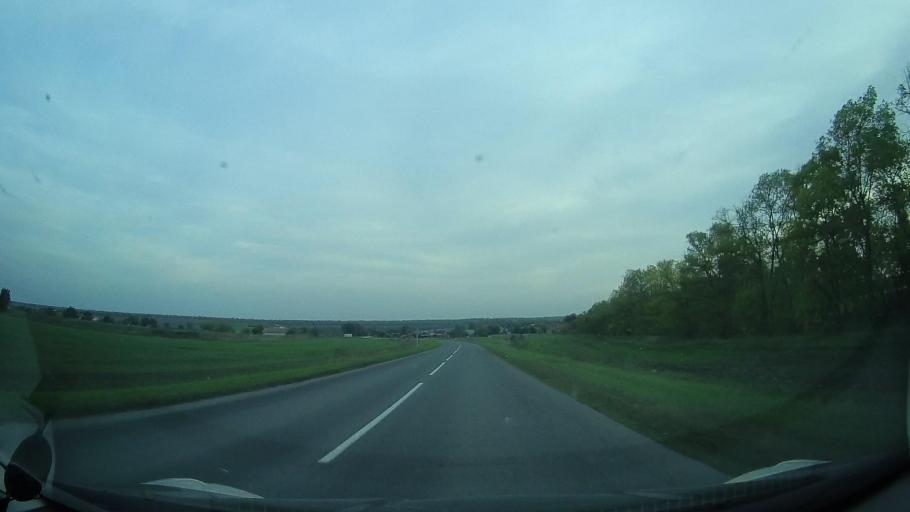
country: RU
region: Rostov
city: Kirovskaya
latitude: 47.0393
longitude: 39.9779
